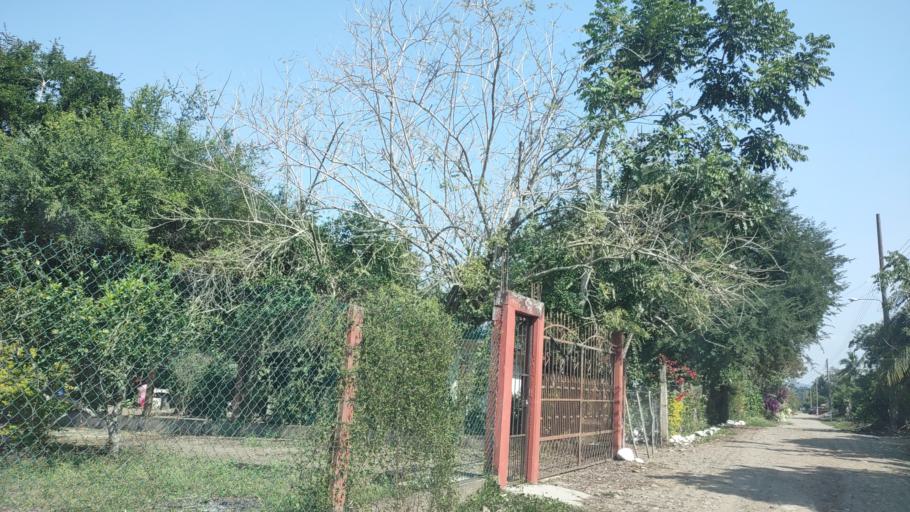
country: MX
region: Puebla
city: Espinal
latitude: 20.2608
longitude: -97.3117
